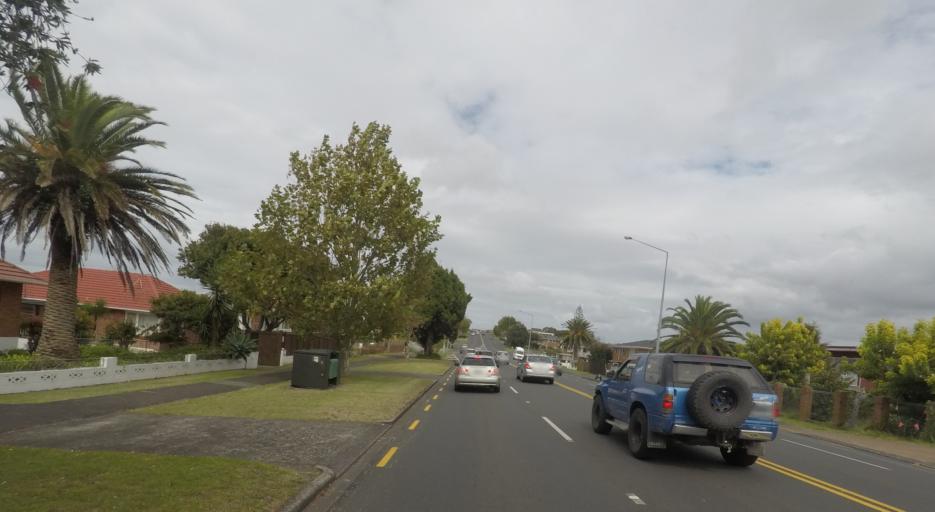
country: NZ
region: Auckland
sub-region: Auckland
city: Rosebank
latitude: -36.8887
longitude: 174.6446
